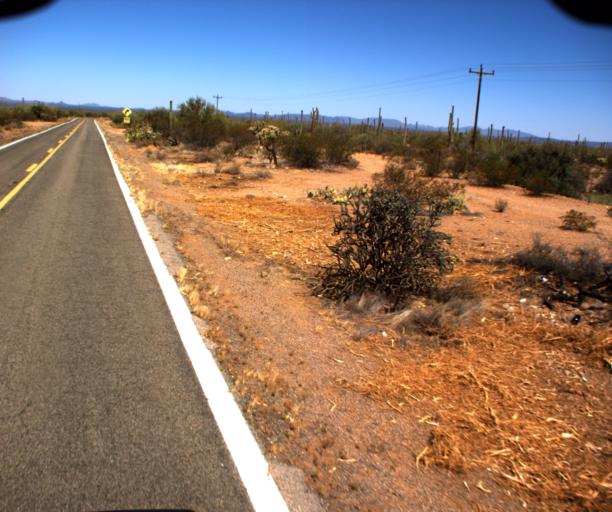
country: US
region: Arizona
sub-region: Pima County
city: Sells
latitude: 32.1775
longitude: -112.2693
